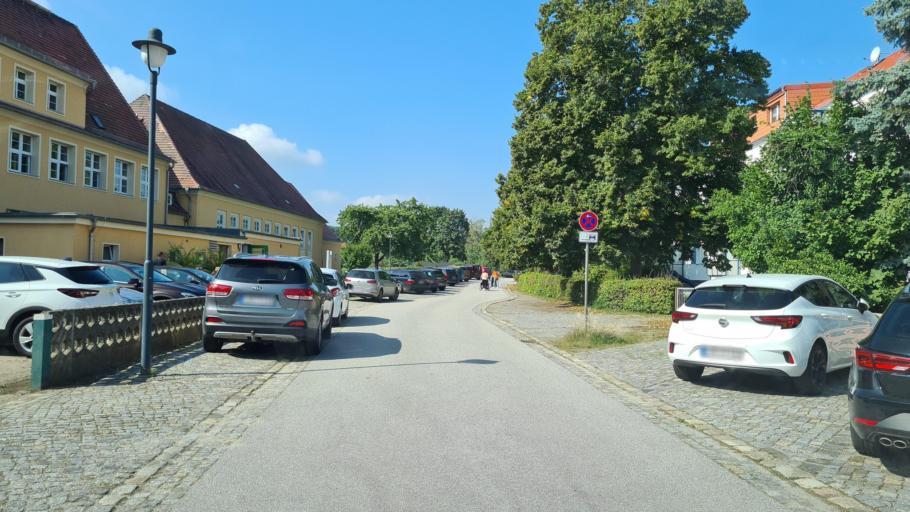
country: DE
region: Brandenburg
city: Luckau
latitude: 51.8557
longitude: 13.7080
